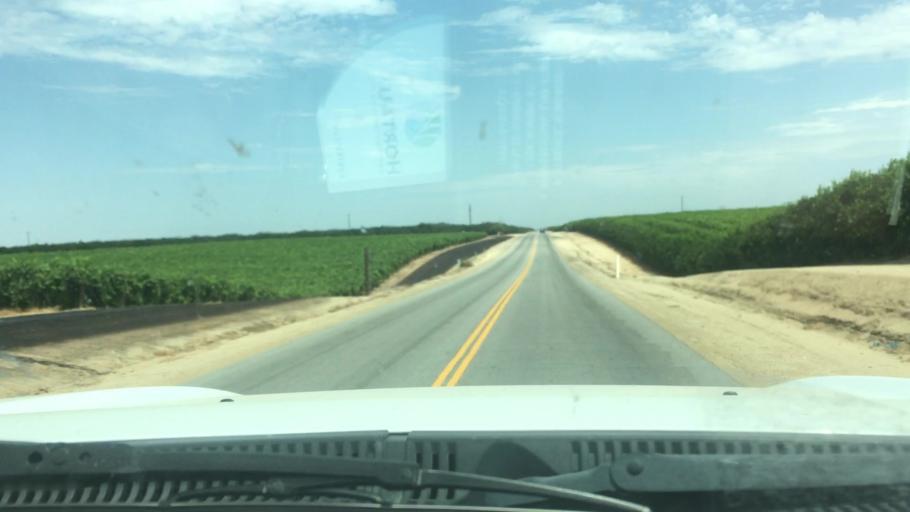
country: US
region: California
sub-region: Kern County
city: McFarland
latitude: 35.5704
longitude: -119.1511
